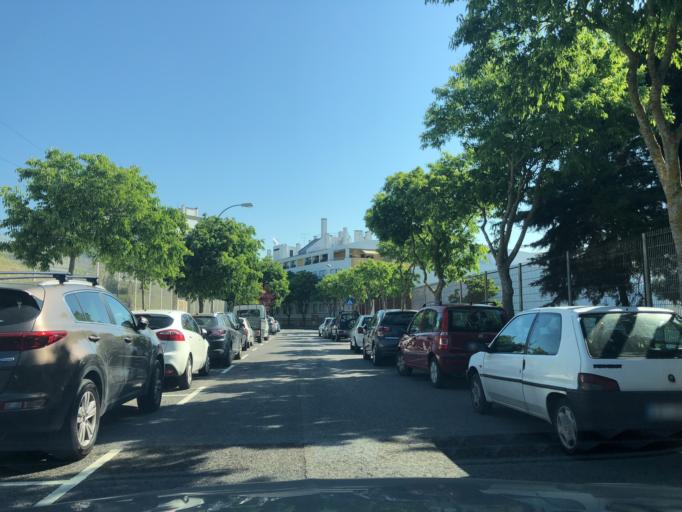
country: PT
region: Lisbon
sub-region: Oeiras
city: Paco de Arcos
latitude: 38.6991
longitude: -9.2962
